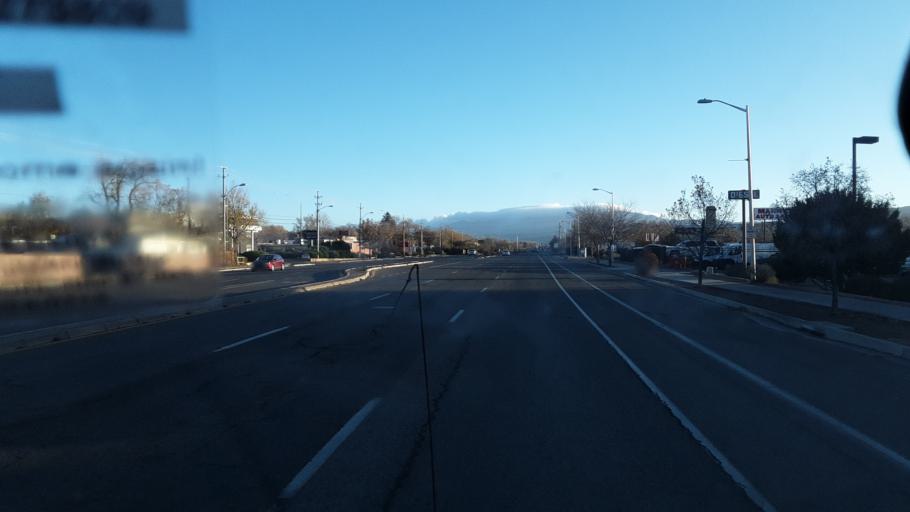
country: US
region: New Mexico
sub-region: Santa Fe County
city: Agua Fria
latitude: 35.6451
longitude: -106.0080
